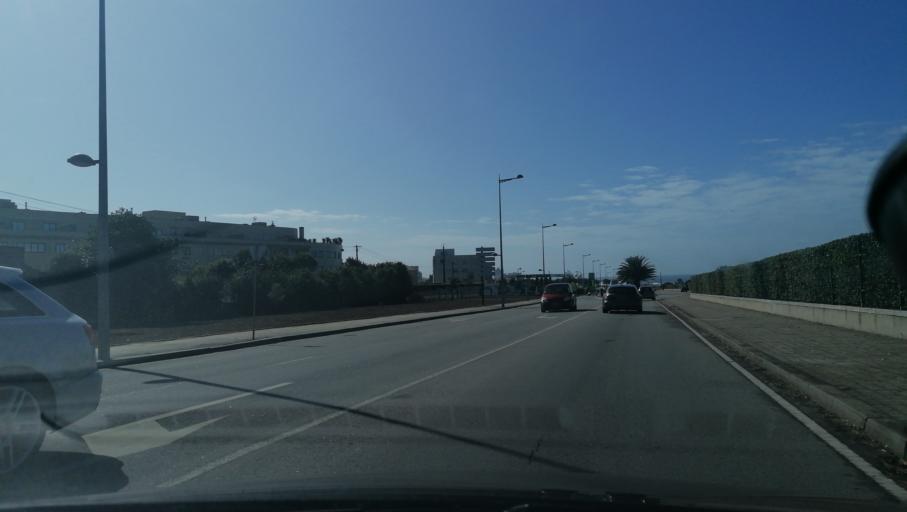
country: PT
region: Porto
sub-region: Vila Nova de Gaia
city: Sao Felix da Marinha
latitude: 41.0295
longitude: -8.6414
